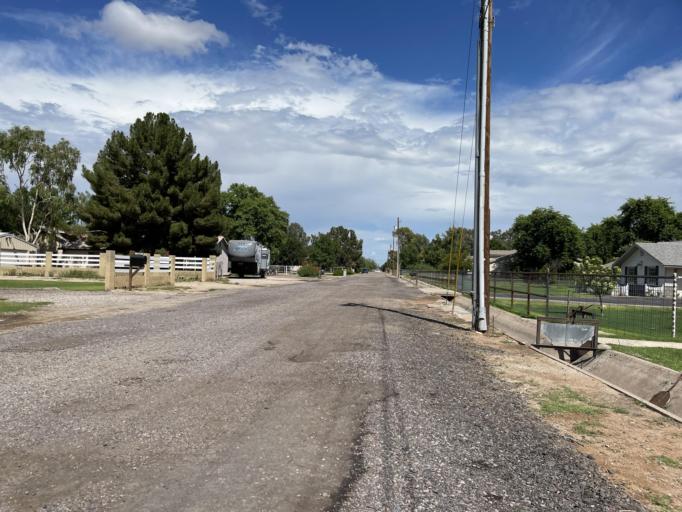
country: US
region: Arizona
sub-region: Maricopa County
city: Sun Lakes
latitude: 33.2298
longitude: -111.8135
